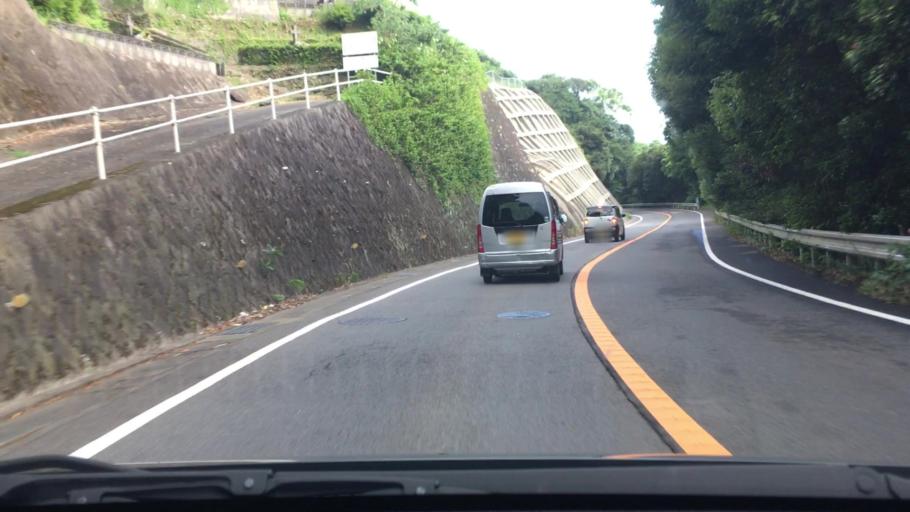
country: JP
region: Nagasaki
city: Togitsu
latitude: 32.8419
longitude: 129.7133
